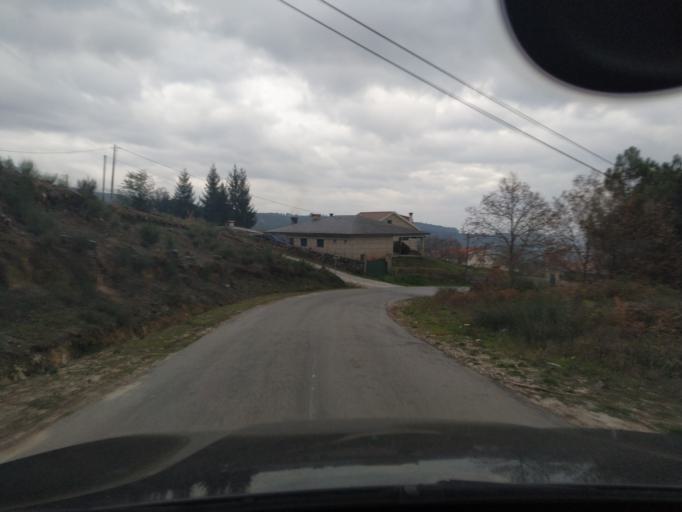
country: PT
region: Vila Real
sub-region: Vila Real
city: Vila Real
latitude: 41.3373
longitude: -7.6596
